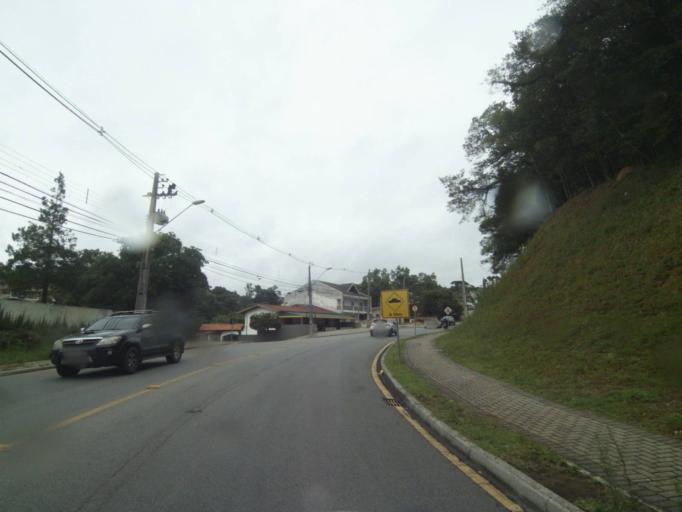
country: BR
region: Parana
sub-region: Curitiba
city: Curitiba
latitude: -25.4247
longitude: -49.3216
